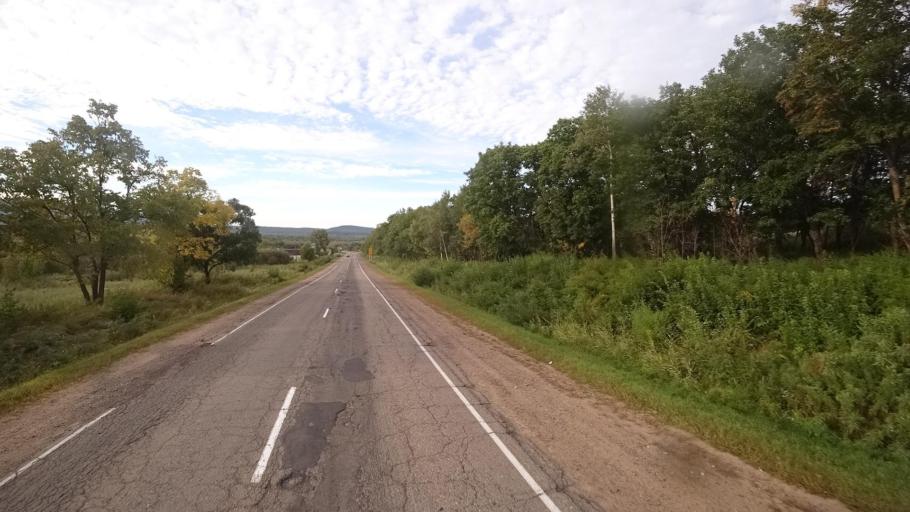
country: RU
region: Primorskiy
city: Yakovlevka
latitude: 44.4136
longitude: 133.4536
